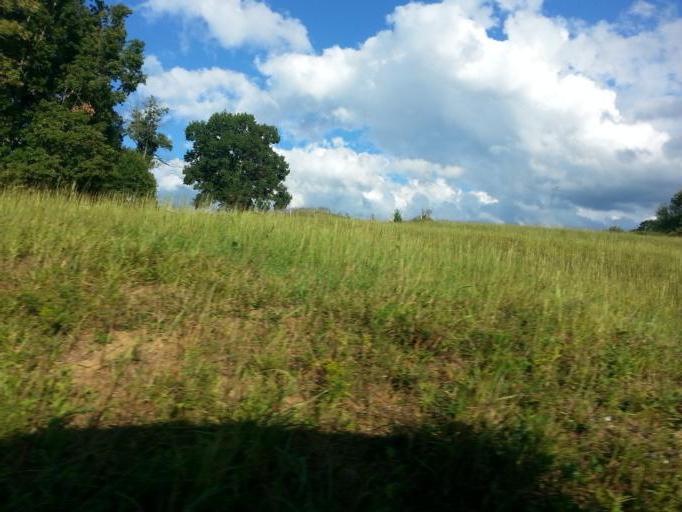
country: US
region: Tennessee
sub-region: Grainger County
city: Blaine
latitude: 36.1595
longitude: -83.7366
